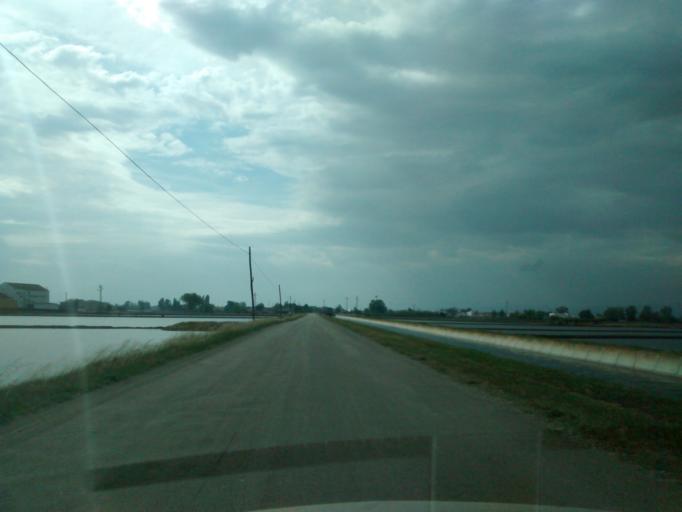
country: ES
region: Catalonia
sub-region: Provincia de Tarragona
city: Deltebre
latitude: 40.7008
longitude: 0.7452
